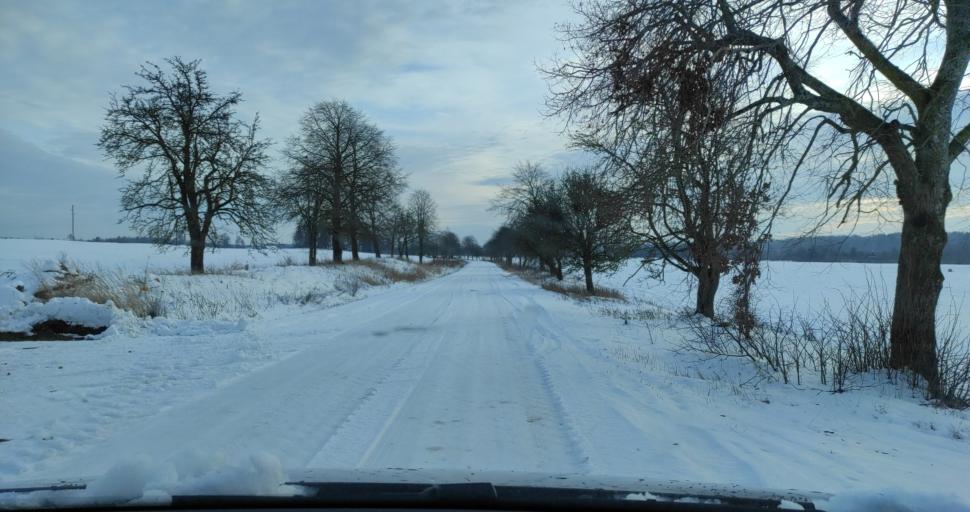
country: LV
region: Kuldigas Rajons
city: Kuldiga
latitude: 56.9534
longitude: 22.0163
